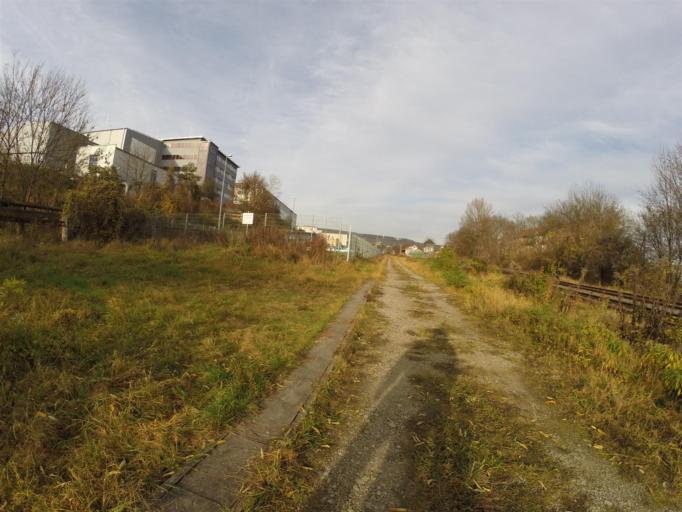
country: DE
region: Thuringia
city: Jena
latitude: 50.9187
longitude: 11.5774
